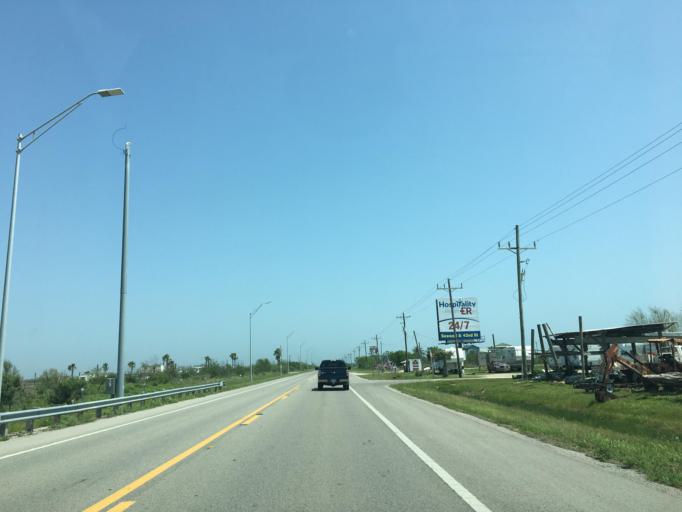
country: US
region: Texas
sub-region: Galveston County
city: Galveston
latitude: 29.3718
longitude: -94.7555
